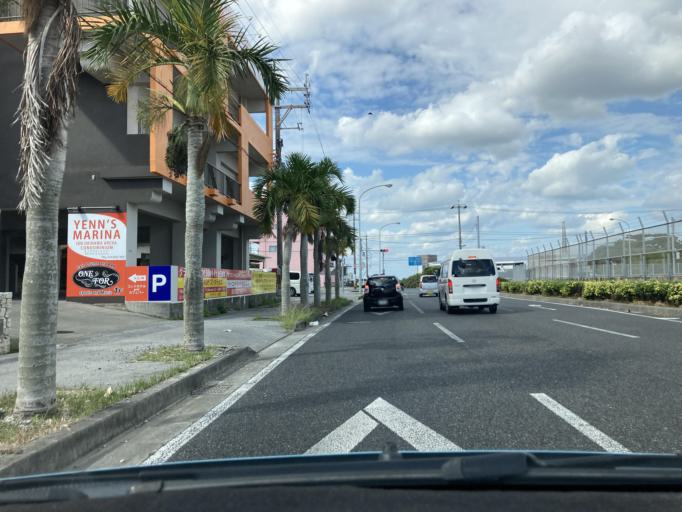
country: JP
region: Okinawa
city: Okinawa
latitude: 26.3296
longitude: 127.7845
